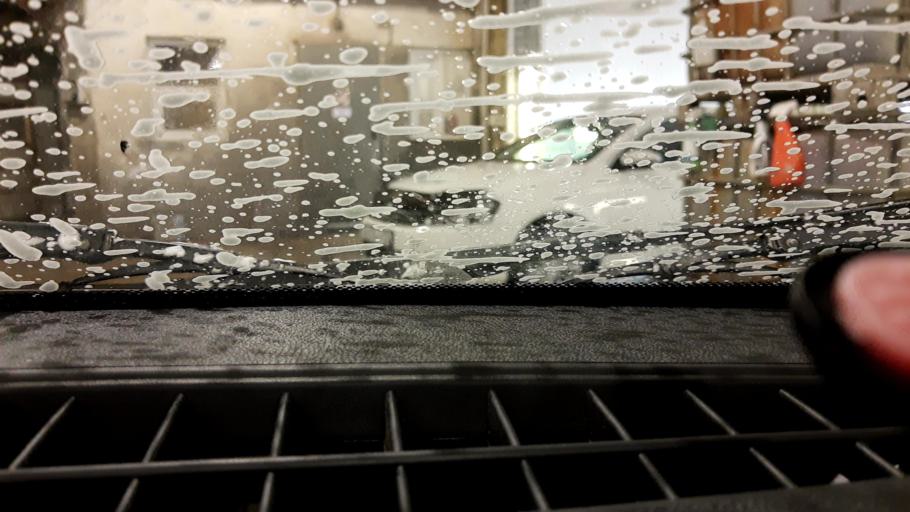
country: RU
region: Bashkortostan
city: Ufa
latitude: 54.7822
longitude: 56.0671
